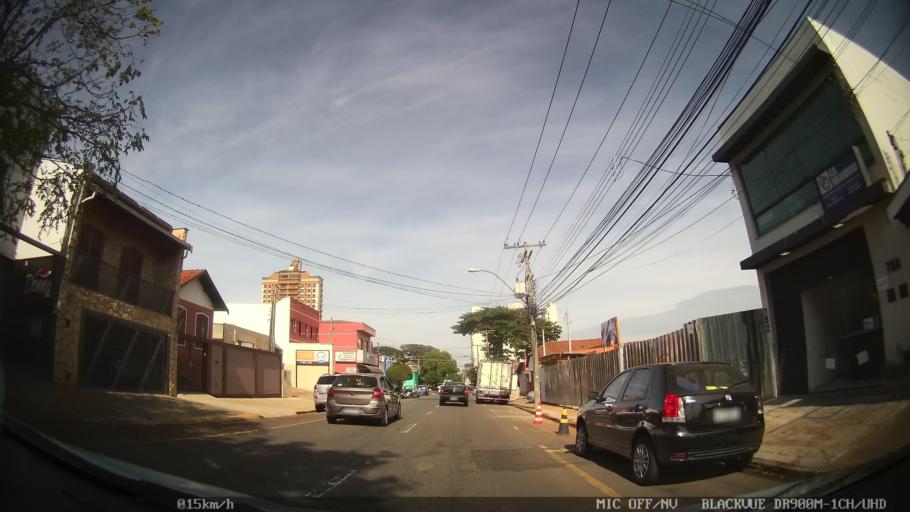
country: BR
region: Sao Paulo
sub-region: Piracicaba
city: Piracicaba
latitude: -22.7137
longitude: -47.6570
